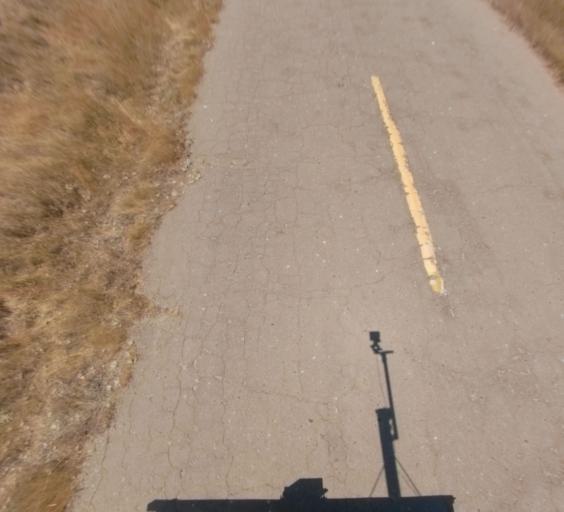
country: US
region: California
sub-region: Madera County
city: Madera Acres
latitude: 37.1007
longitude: -120.0013
